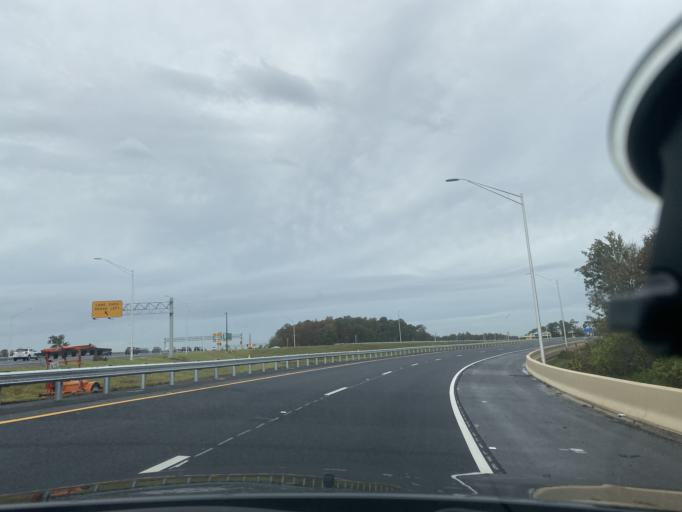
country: US
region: Florida
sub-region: Orange County
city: Alafaya
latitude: 28.5480
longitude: -81.2194
